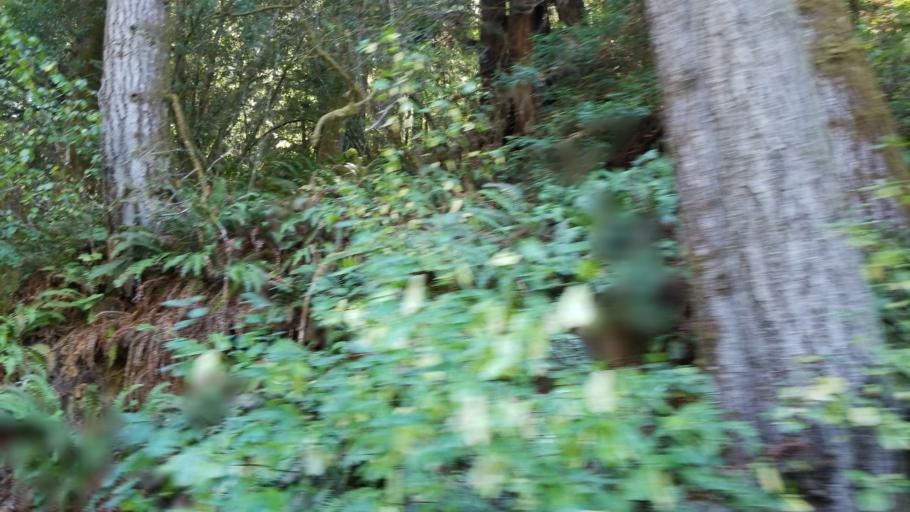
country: US
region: California
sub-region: Mendocino County
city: Fort Bragg
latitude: 39.4474
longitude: -123.7704
